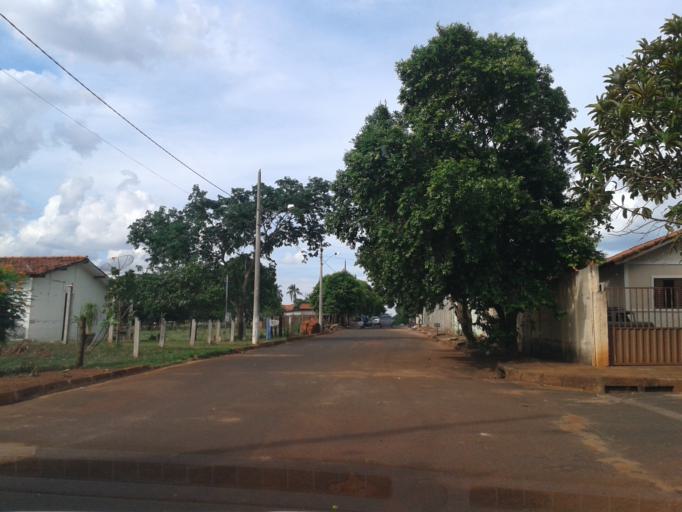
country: BR
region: Minas Gerais
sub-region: Centralina
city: Centralina
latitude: -18.7224
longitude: -49.2061
